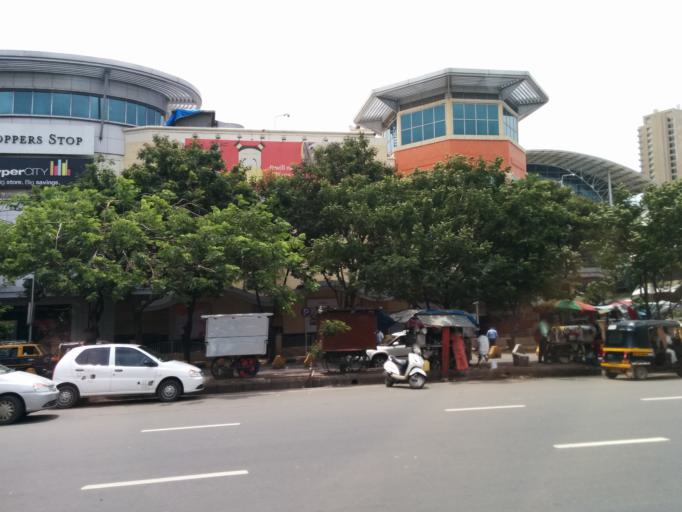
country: IN
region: Maharashtra
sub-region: Thane
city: Thane
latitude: 19.2076
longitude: 72.9719
